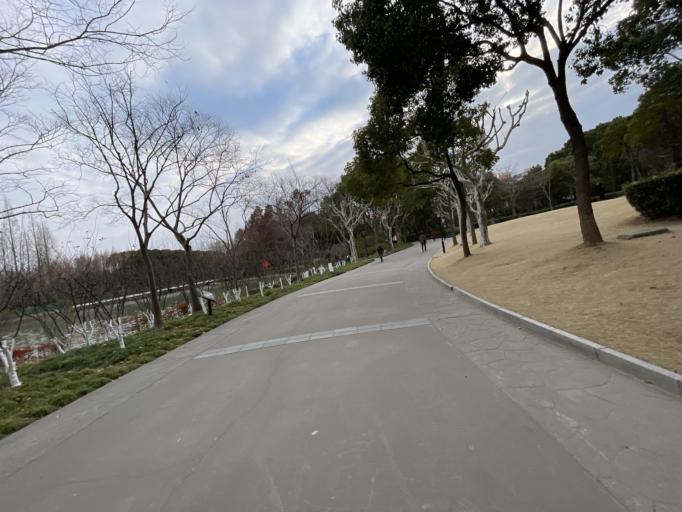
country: CN
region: Shanghai Shi
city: Yangpu
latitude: 31.2940
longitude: 121.5235
